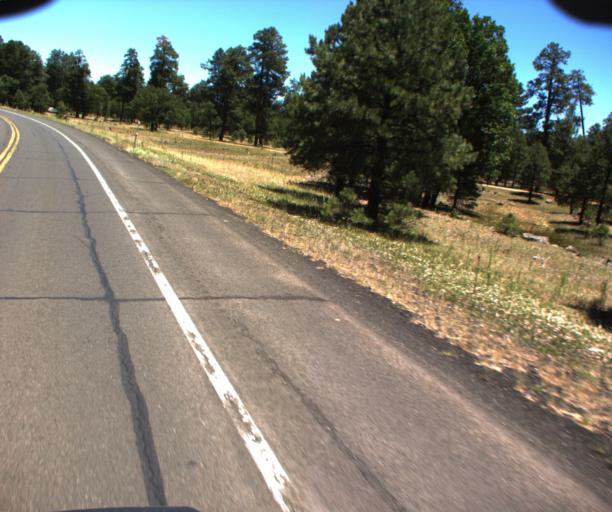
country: US
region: Arizona
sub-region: Gila County
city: Pine
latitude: 34.5528
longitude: -111.2910
